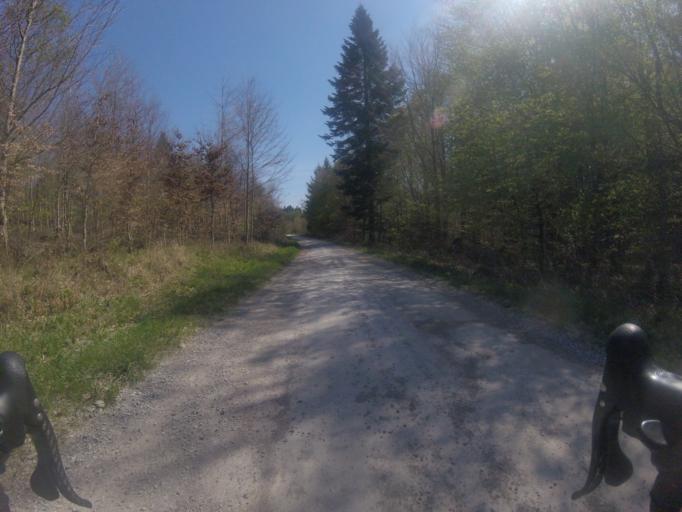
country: CH
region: Fribourg
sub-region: Sense District
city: Flamatt
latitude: 46.9121
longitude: 7.3135
